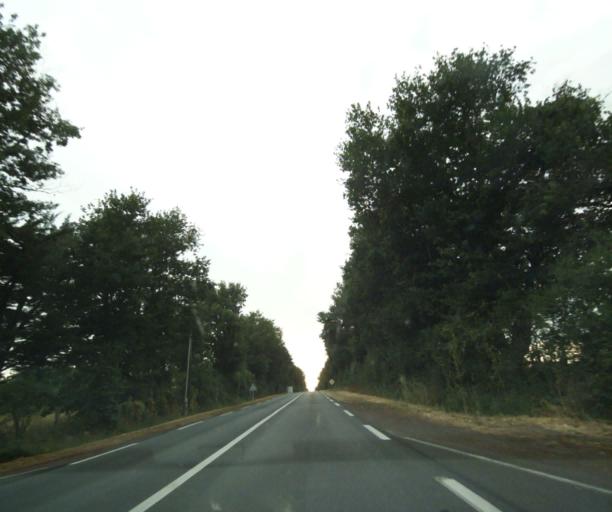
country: FR
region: Pays de la Loire
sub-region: Departement de la Vendee
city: Avrille
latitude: 46.4624
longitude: -1.4566
